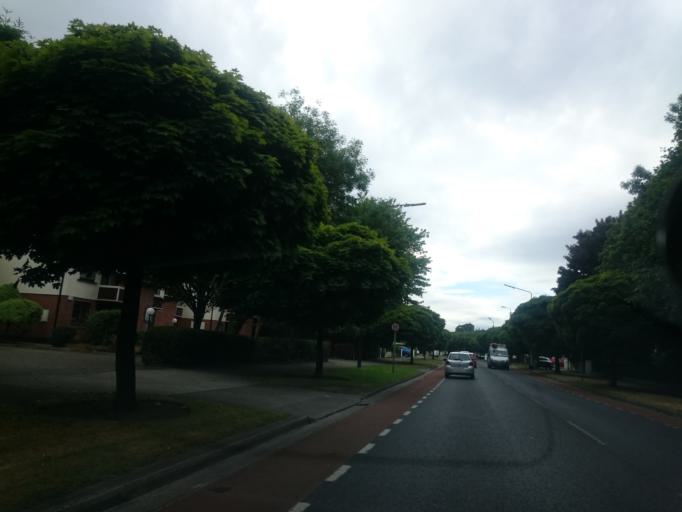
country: IE
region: Leinster
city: Rathgar
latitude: 53.3037
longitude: -6.2727
